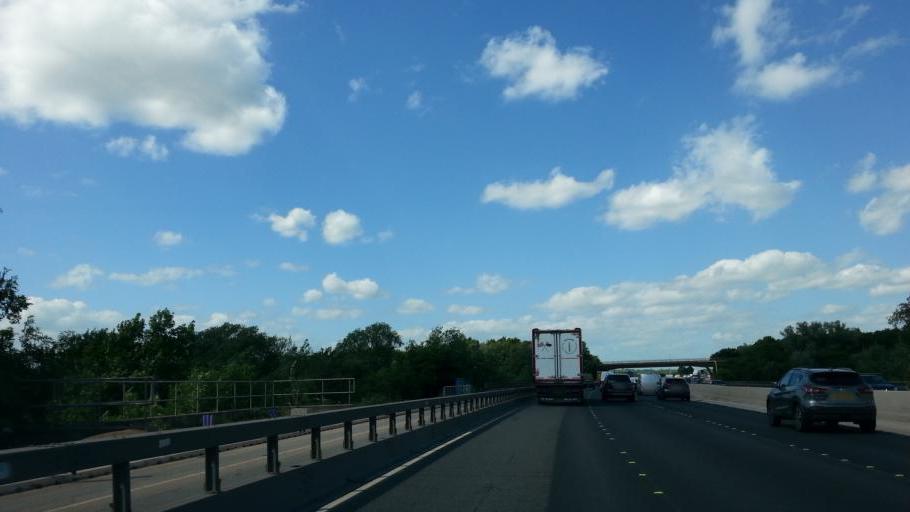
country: GB
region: England
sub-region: Derbyshire
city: Long Eaton
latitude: 52.8787
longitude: -1.3109
